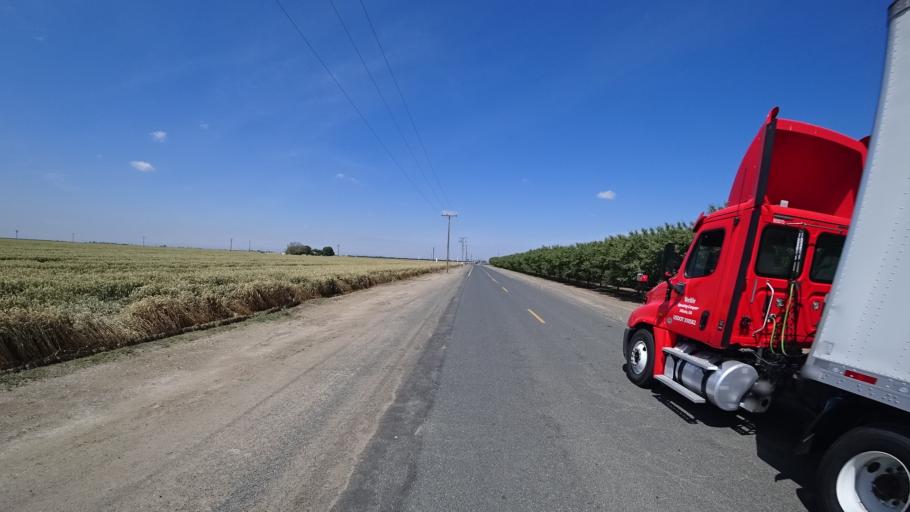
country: US
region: California
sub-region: Tulare County
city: Goshen
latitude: 36.2691
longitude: -119.5074
